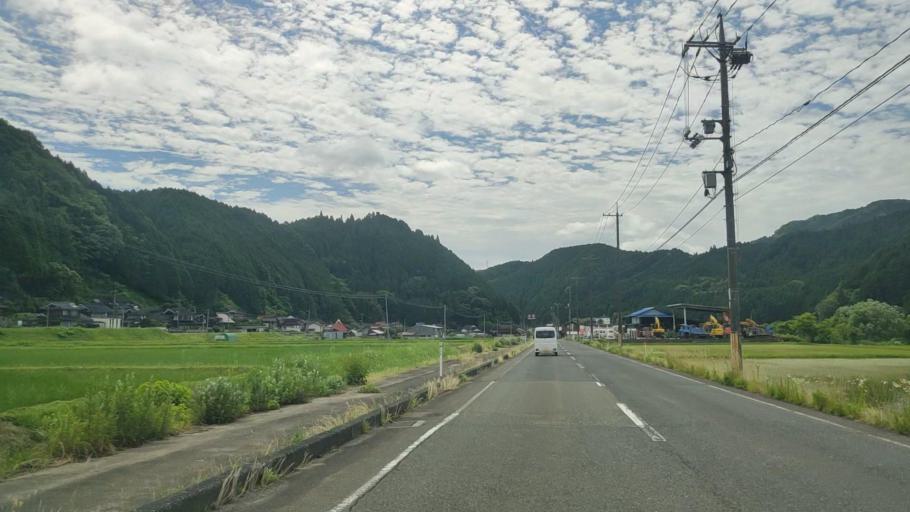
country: JP
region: Okayama
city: Niimi
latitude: 35.1604
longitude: 133.6101
